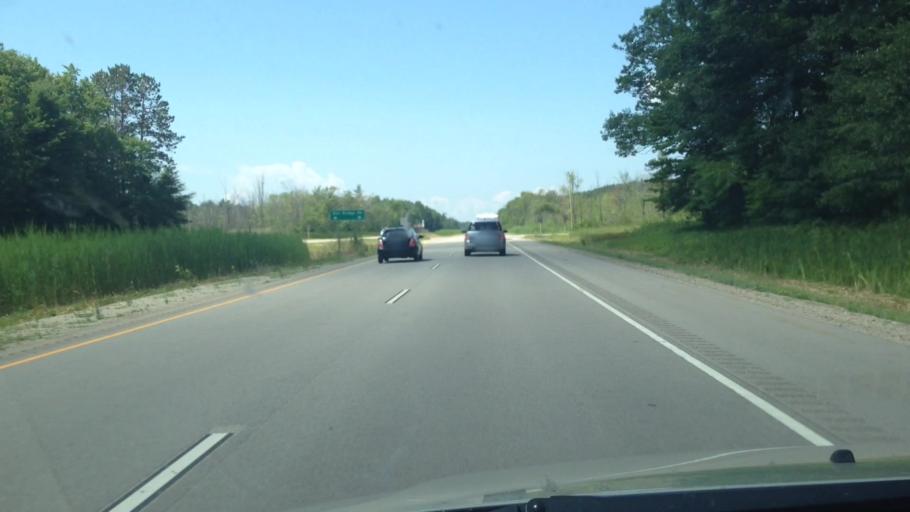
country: US
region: Wisconsin
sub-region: Oconto County
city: Oconto
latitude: 44.8128
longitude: -87.9543
